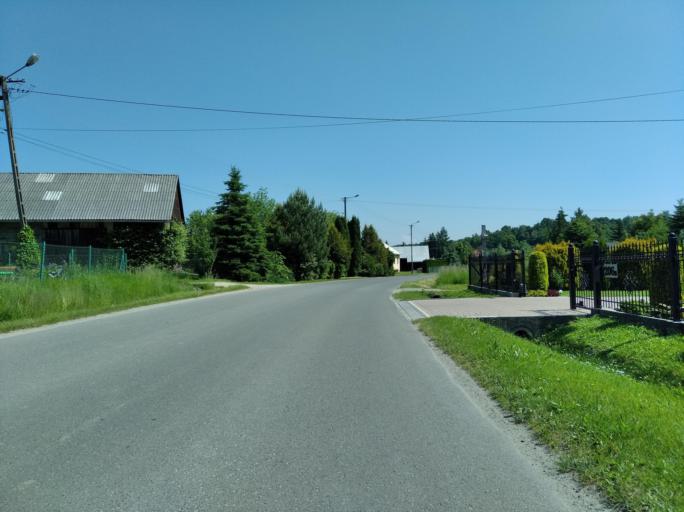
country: PL
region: Subcarpathian Voivodeship
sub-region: Powiat ropczycko-sedziszowski
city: Zagorzyce
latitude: 50.0139
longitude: 21.6726
